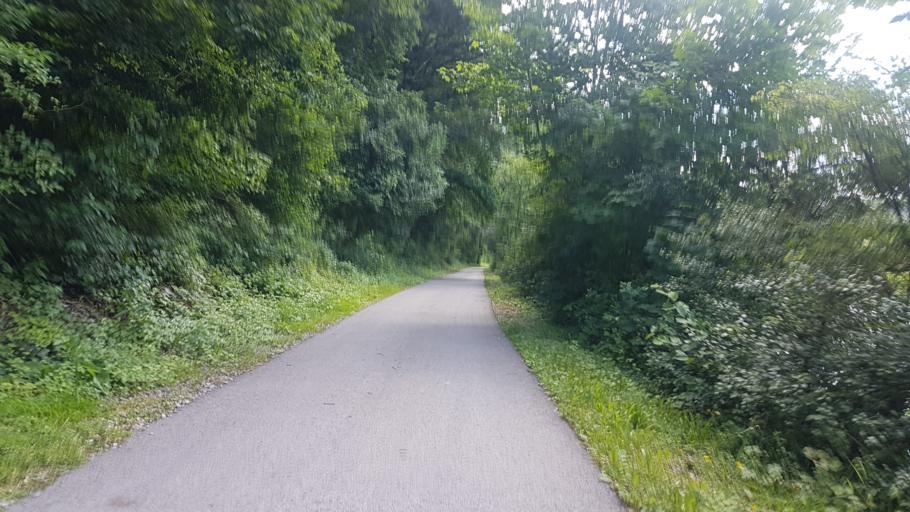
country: DE
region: Bavaria
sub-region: Regierungsbezirk Mittelfranken
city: Pappenheim
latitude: 48.9241
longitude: 10.9827
